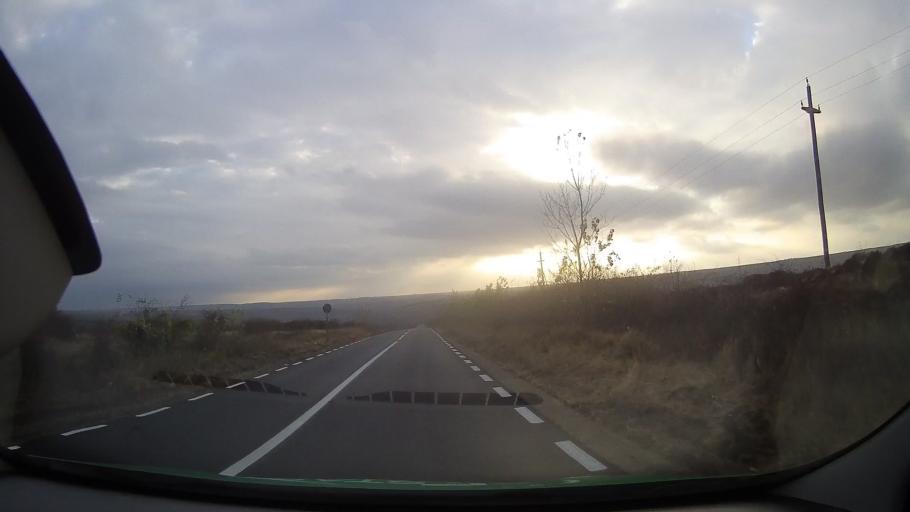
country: RO
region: Constanta
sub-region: Comuna Adamclisi
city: Adamclisi
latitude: 44.0647
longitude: 27.9726
